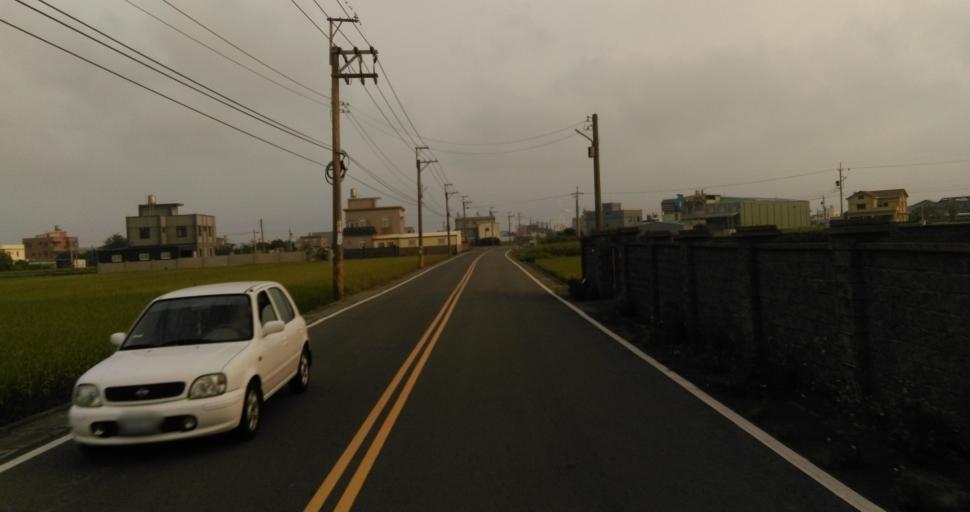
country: TW
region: Taiwan
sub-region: Hsinchu
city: Zhubei
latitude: 24.8715
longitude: 120.9574
